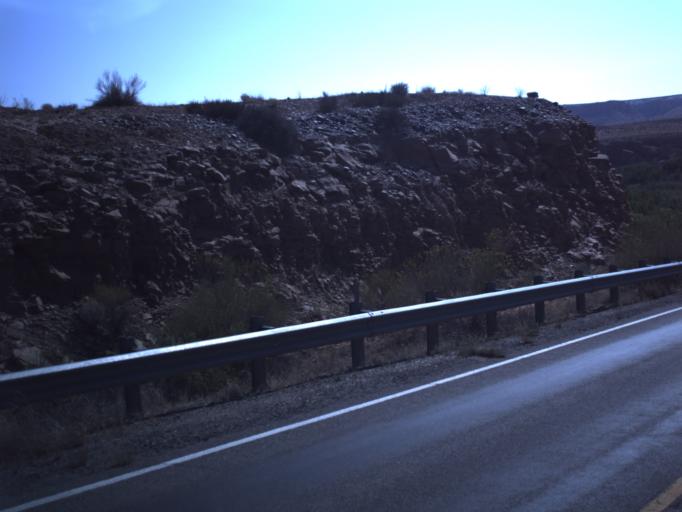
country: US
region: Utah
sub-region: San Juan County
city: Blanding
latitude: 37.2604
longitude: -109.6216
